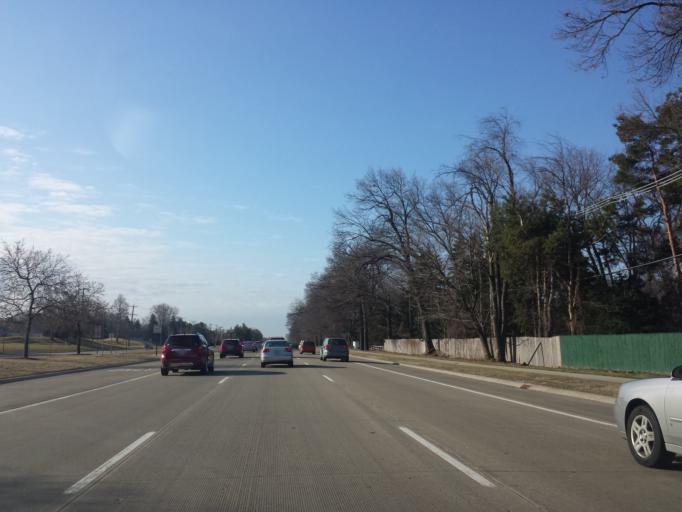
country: US
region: Michigan
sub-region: Oakland County
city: Franklin
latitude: 42.5530
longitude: -83.2854
